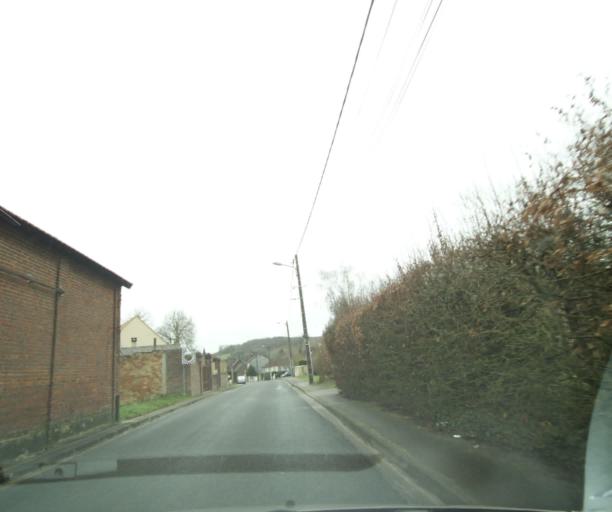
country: FR
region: Picardie
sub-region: Departement de l'Oise
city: Noyon
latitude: 49.5952
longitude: 3.0131
